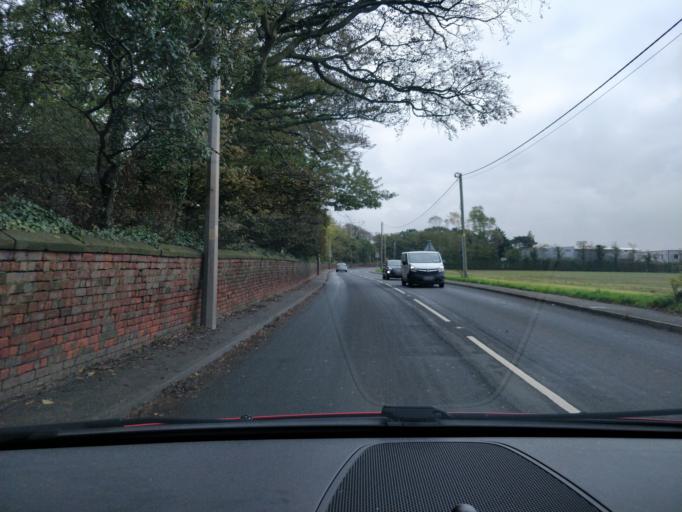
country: GB
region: England
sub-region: Lancashire
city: Ormskirk
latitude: 53.6089
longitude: -2.9337
